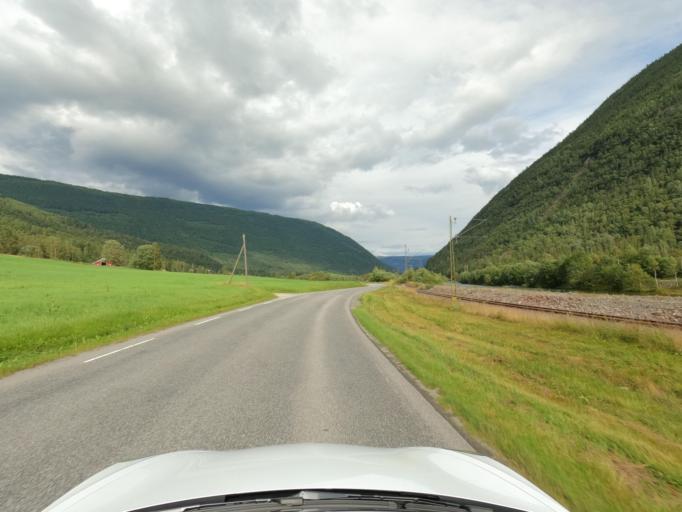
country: NO
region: Telemark
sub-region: Tinn
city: Rjukan
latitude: 59.9184
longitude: 8.7307
